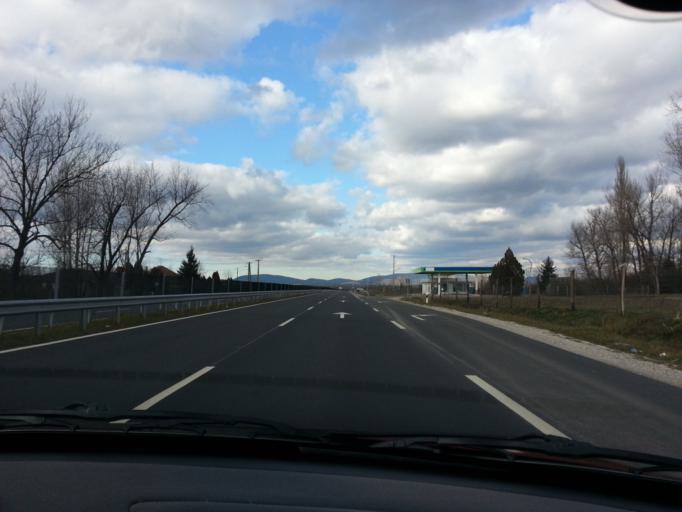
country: HU
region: Nograd
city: Jobbagyi
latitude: 47.8352
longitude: 19.6808
